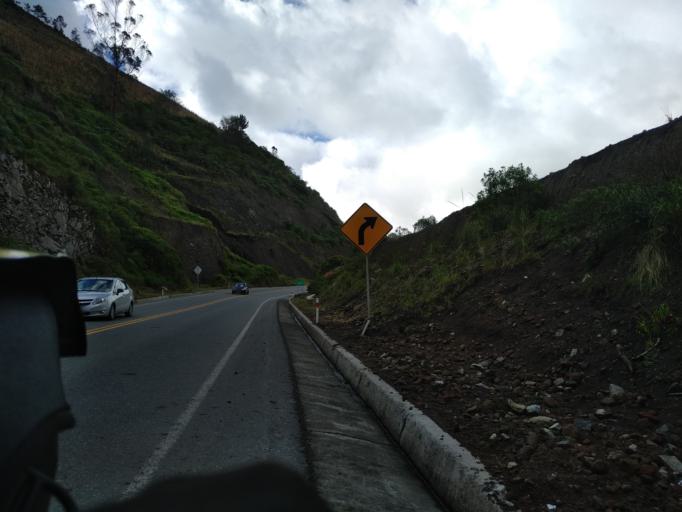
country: EC
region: Tungurahua
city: Banos
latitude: -1.4779
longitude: -78.5183
